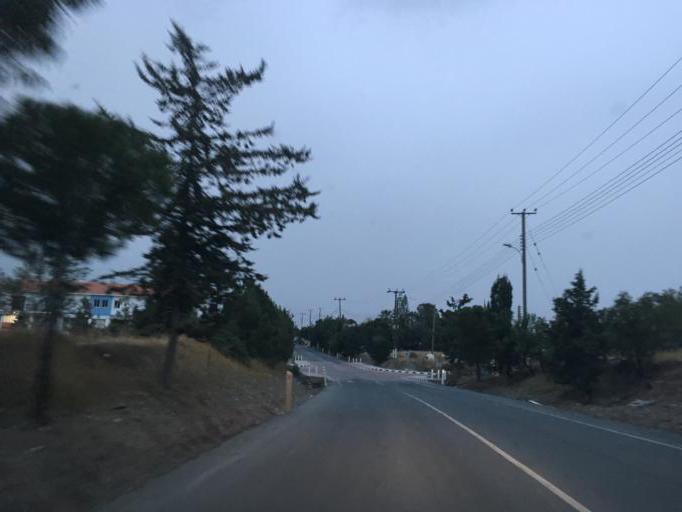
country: CY
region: Limassol
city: Parekklisha
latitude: 34.7411
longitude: 33.1562
